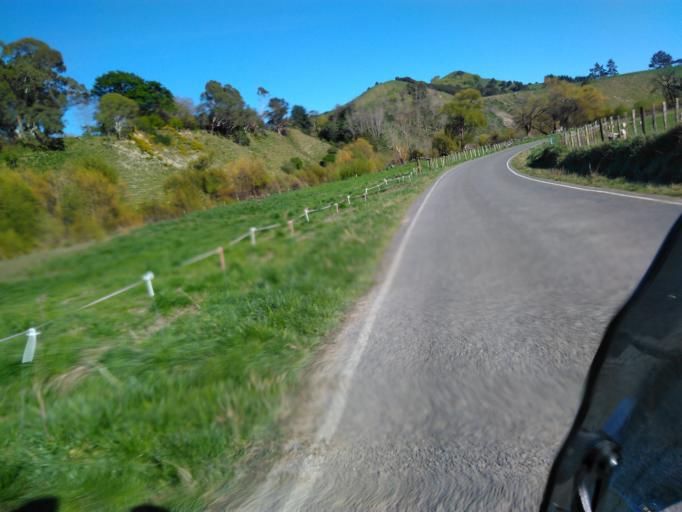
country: NZ
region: Gisborne
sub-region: Gisborne District
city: Gisborne
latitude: -38.4515
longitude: 177.7643
